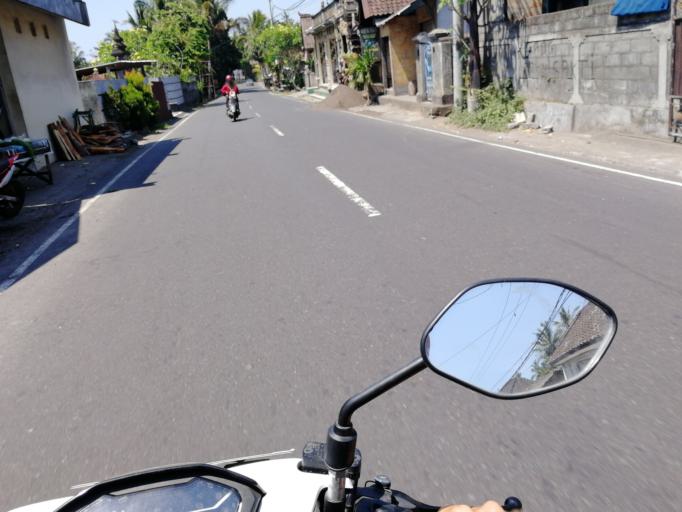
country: ID
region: Bali
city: Banjar Ababi
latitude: -8.3988
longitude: 115.5959
